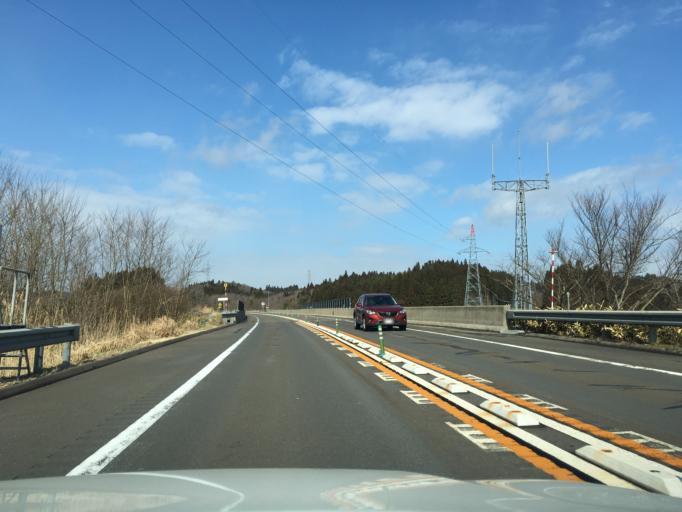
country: JP
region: Akita
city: Akita
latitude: 39.7389
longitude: 140.1714
